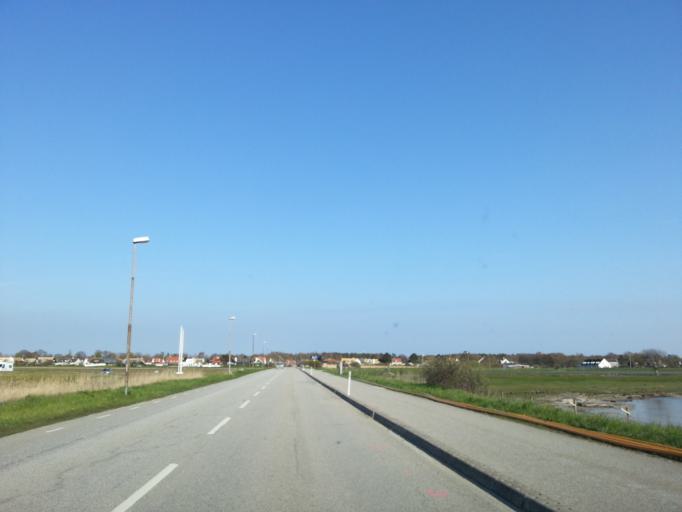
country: SE
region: Skane
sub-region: Vellinge Kommun
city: Skanor med Falsterbo
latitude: 55.4157
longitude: 12.8340
